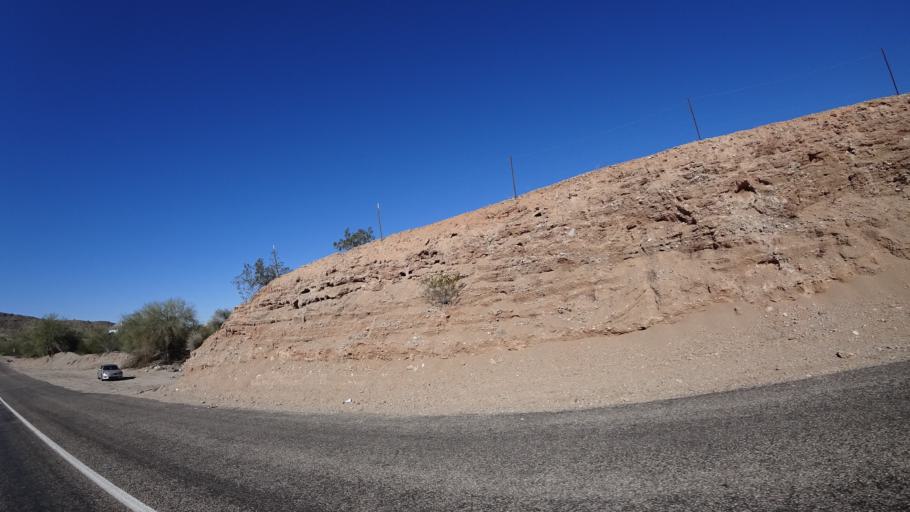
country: US
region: Arizona
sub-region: Maricopa County
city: Goodyear
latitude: 33.3755
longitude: -112.3608
